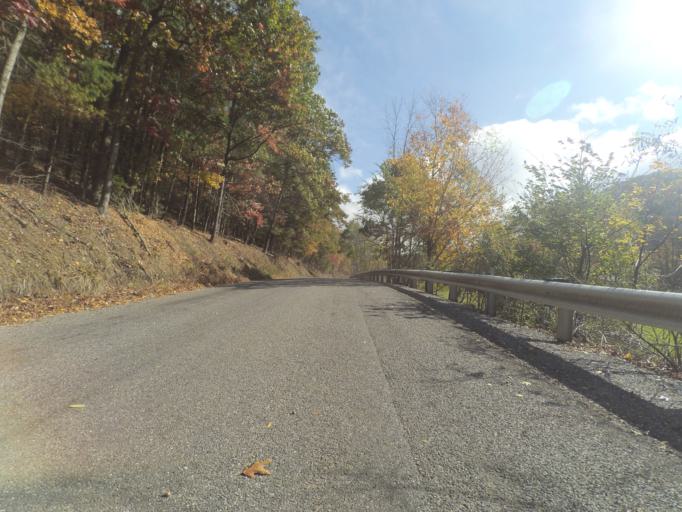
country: US
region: Pennsylvania
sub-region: Centre County
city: Park Forest Village
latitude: 40.9101
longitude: -77.9205
